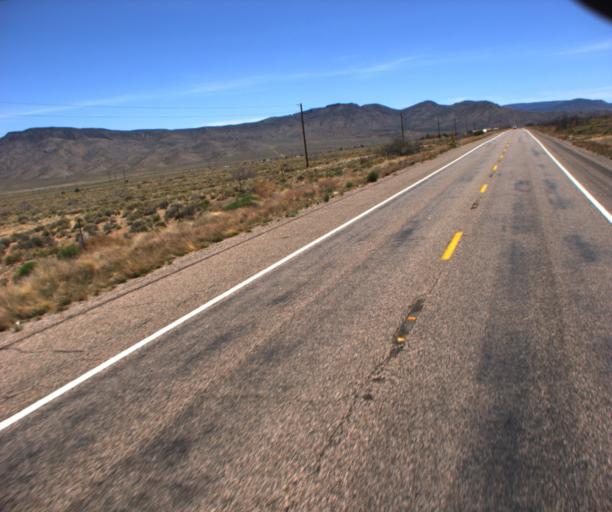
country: US
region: Arizona
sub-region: Mohave County
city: New Kingman-Butler
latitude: 35.4157
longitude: -113.7914
